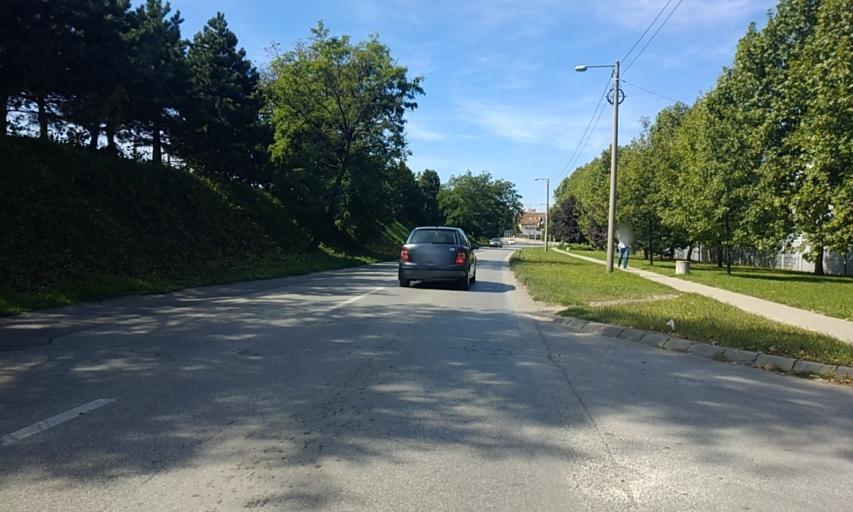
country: BA
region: Republika Srpska
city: Banja Luka
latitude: 44.7886
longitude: 17.2036
